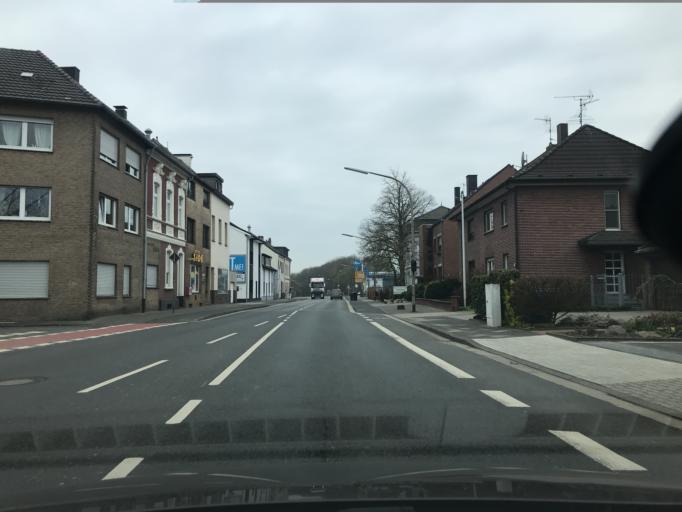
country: DE
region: North Rhine-Westphalia
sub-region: Regierungsbezirk Dusseldorf
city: Viersen
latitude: 51.2619
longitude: 6.3367
